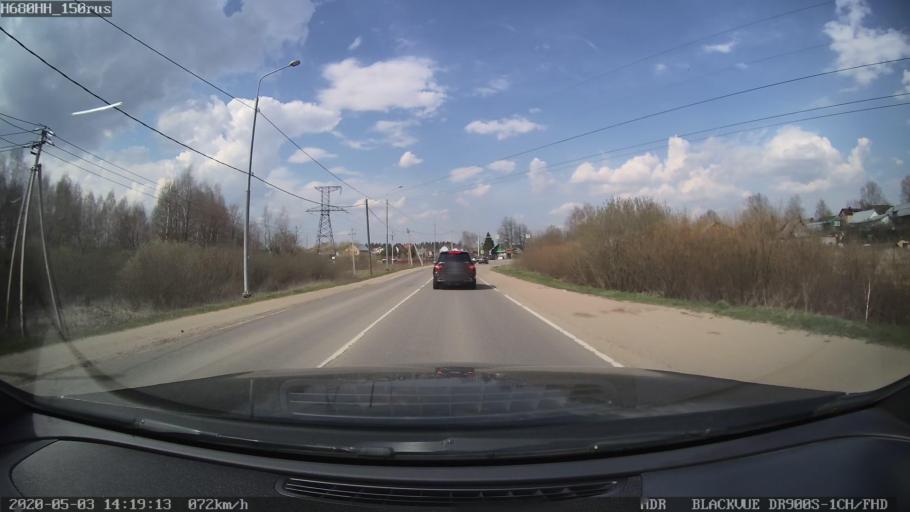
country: RU
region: Moskovskaya
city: Solnechnogorsk
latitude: 56.2297
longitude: 36.9679
